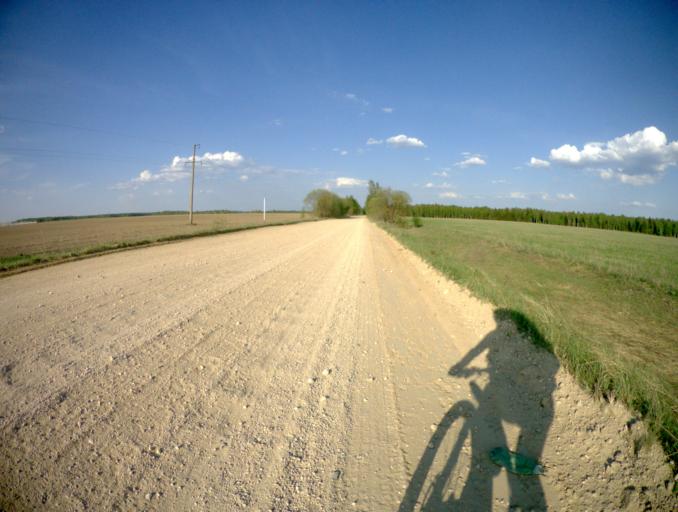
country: RU
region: Vladimir
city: Mstera
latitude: 56.5441
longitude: 41.6540
